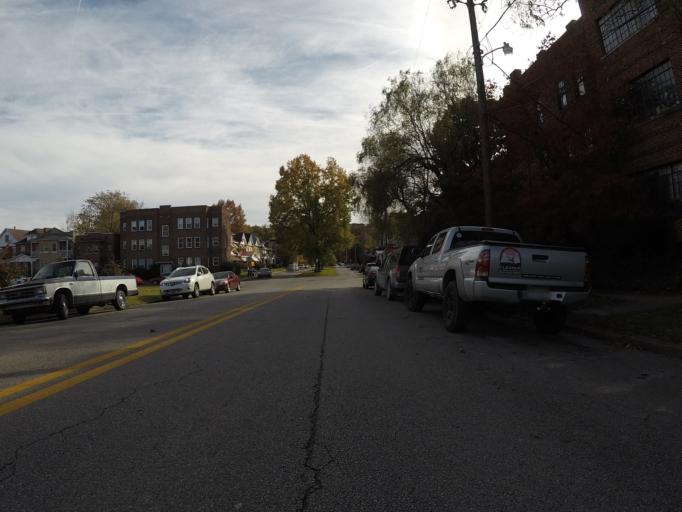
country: US
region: West Virginia
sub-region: Cabell County
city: Huntington
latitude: 38.4117
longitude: -82.4395
